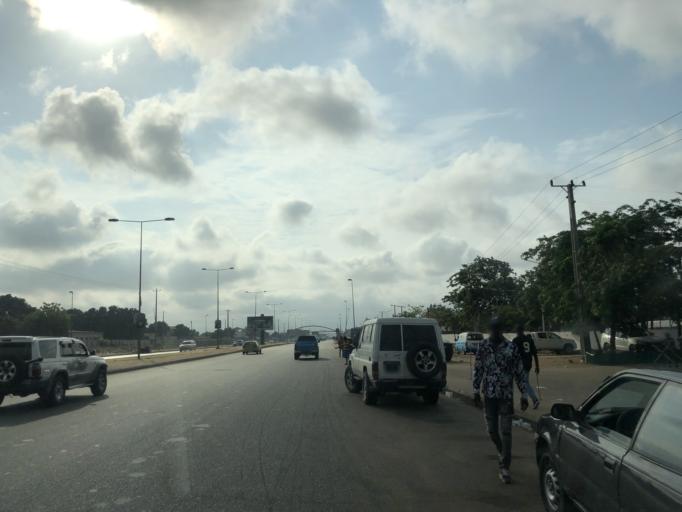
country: AO
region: Luanda
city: Luanda
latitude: -8.9151
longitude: 13.3899
